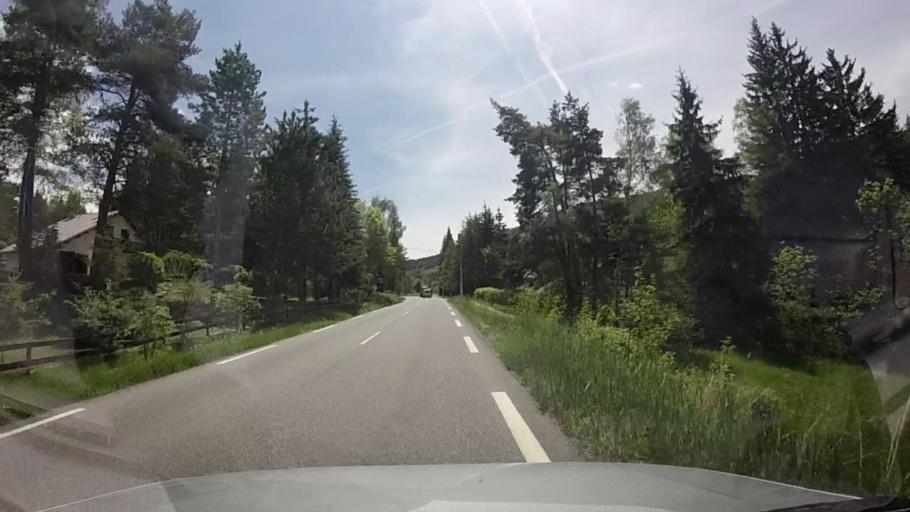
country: FR
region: Provence-Alpes-Cote d'Azur
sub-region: Departement des Alpes-de-Haute-Provence
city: Seyne-les-Alpes
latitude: 44.3311
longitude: 6.3909
